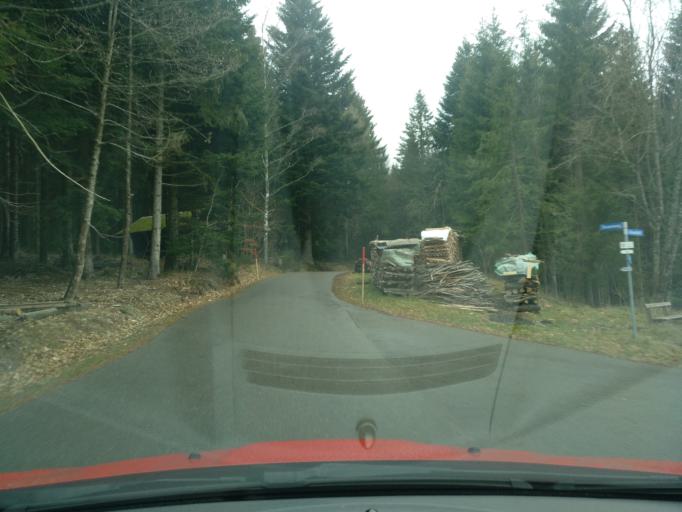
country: DE
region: Baden-Wuerttemberg
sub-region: Freiburg Region
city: Sankt Georgen im Schwarzwald
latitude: 48.1095
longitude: 8.3320
